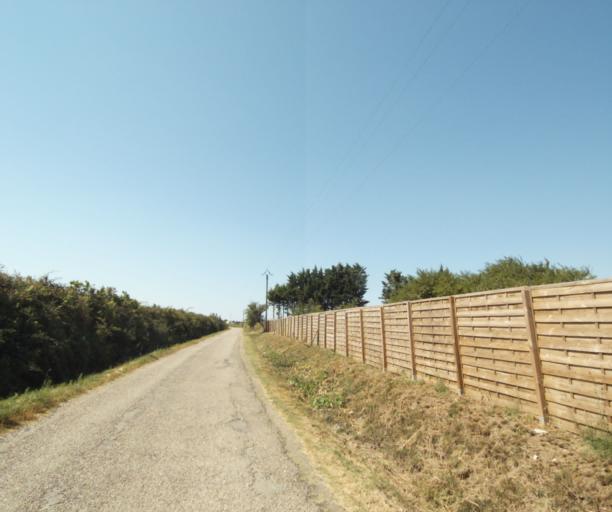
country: FR
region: Languedoc-Roussillon
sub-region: Departement de l'Herault
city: Marsillargues
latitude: 43.6545
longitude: 4.1648
